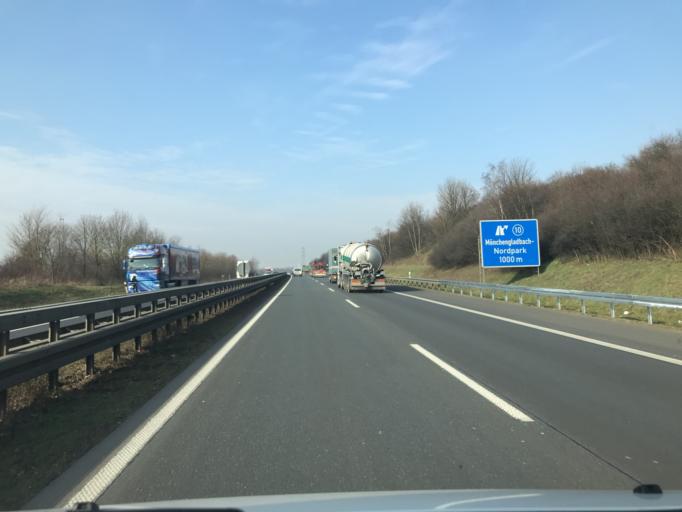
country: DE
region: North Rhine-Westphalia
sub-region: Regierungsbezirk Dusseldorf
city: Monchengladbach
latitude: 51.1847
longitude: 6.3918
